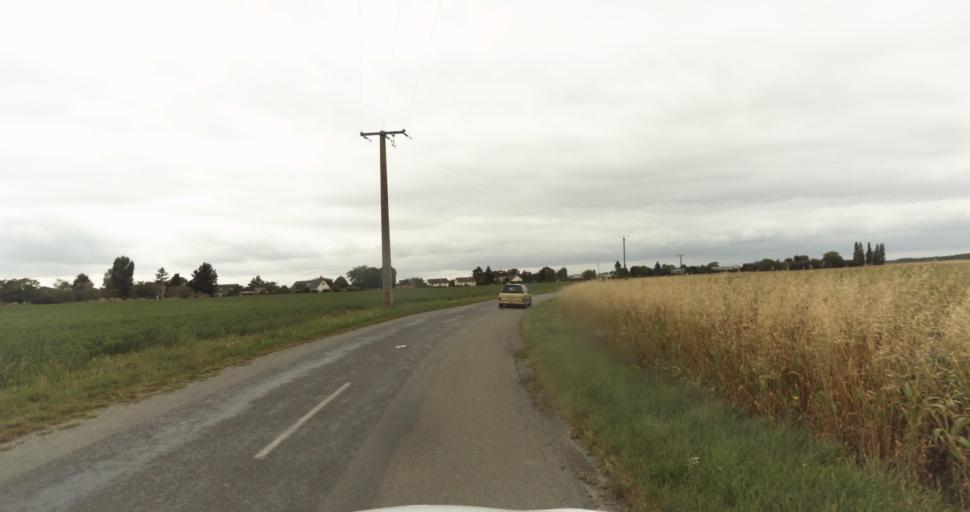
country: FR
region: Haute-Normandie
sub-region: Departement de l'Eure
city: Arnieres-sur-Iton
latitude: 48.9517
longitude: 1.1278
